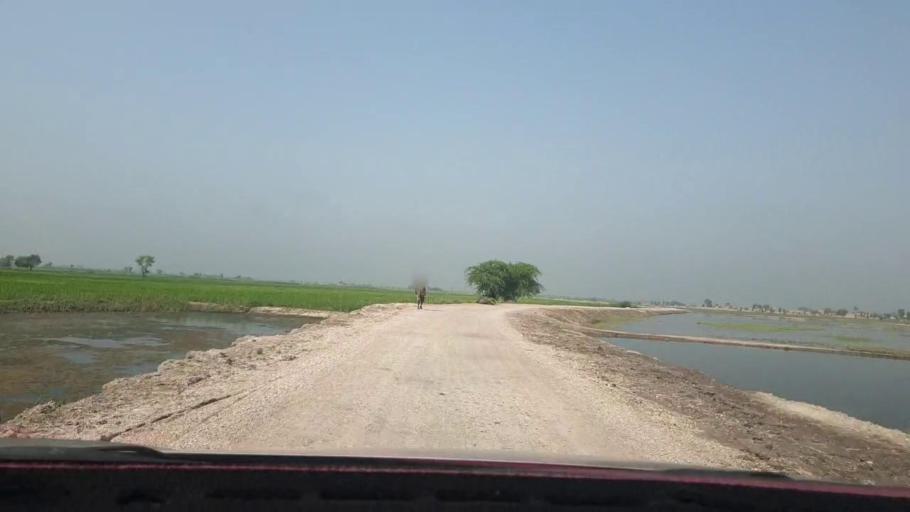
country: PK
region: Sindh
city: Nasirabad
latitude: 27.4365
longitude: 67.9705
